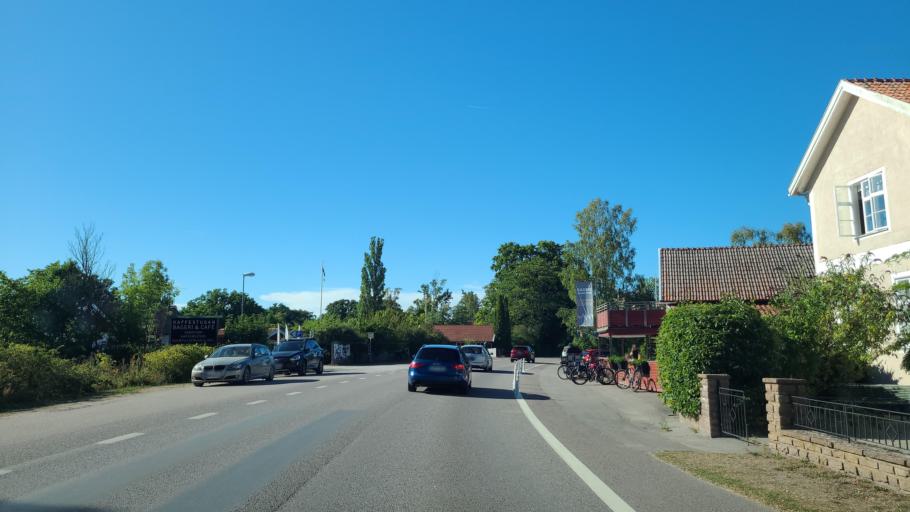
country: SE
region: Kalmar
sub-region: Borgholms Kommun
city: Borgholm
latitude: 57.2459
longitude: 17.0588
